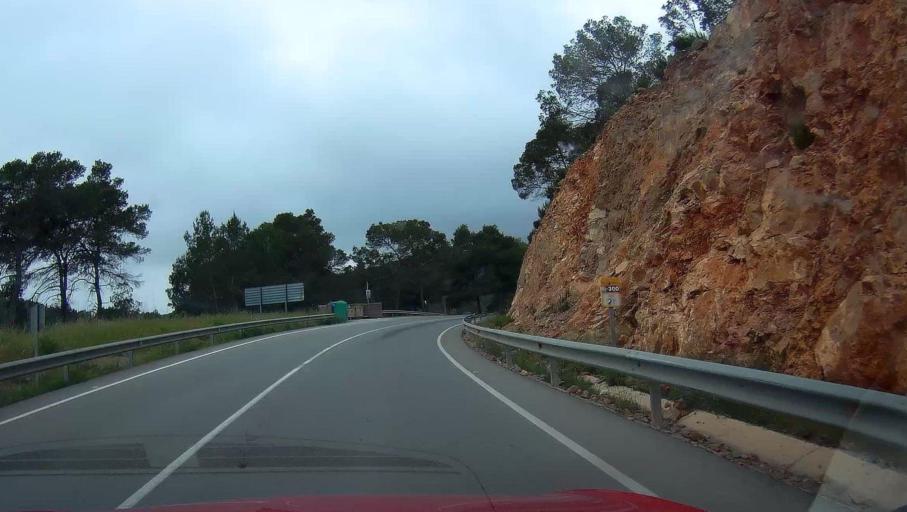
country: ES
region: Balearic Islands
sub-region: Illes Balears
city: Sant Joan de Labritja
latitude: 39.0761
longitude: 1.5055
